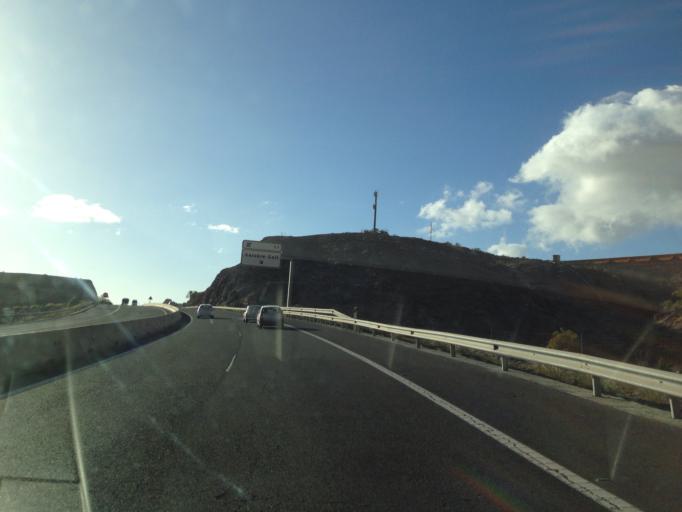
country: ES
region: Canary Islands
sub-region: Provincia de Las Palmas
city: Maspalomas
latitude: 27.7713
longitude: -15.6376
